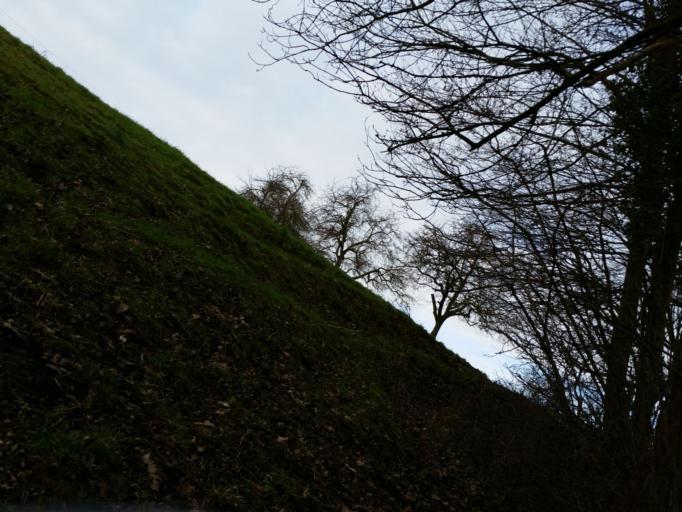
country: CH
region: Thurgau
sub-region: Arbon District
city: Salmsach
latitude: 47.5504
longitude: 9.3536
